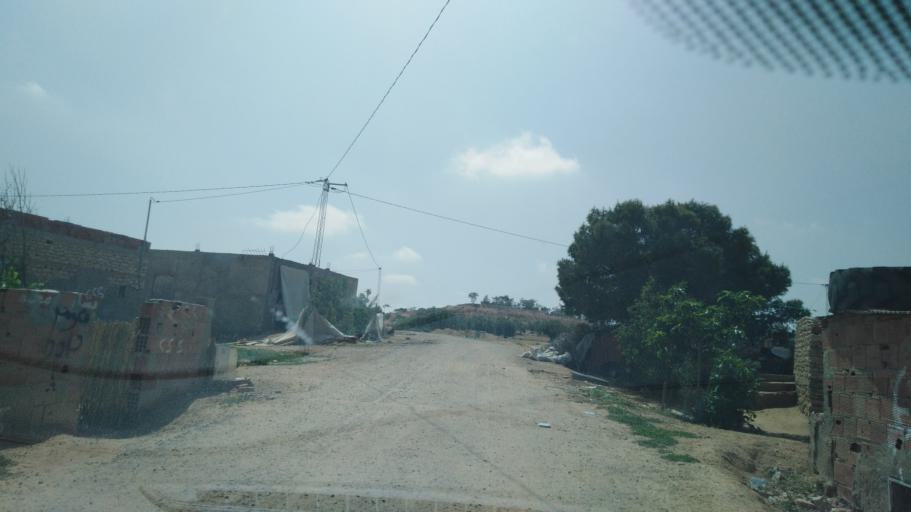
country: TN
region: Safaqis
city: Sfax
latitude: 34.7287
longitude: 10.5683
